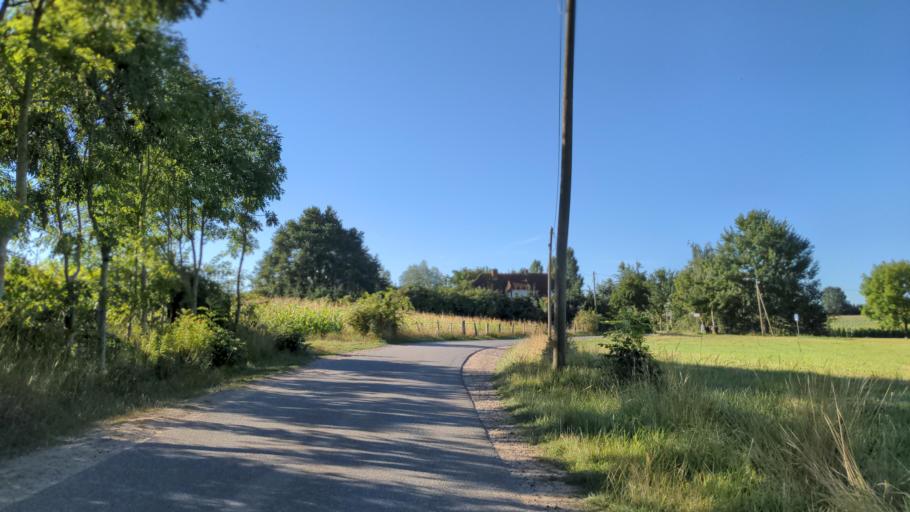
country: DE
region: Mecklenburg-Vorpommern
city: Kalkhorst
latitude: 53.9589
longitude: 11.0082
